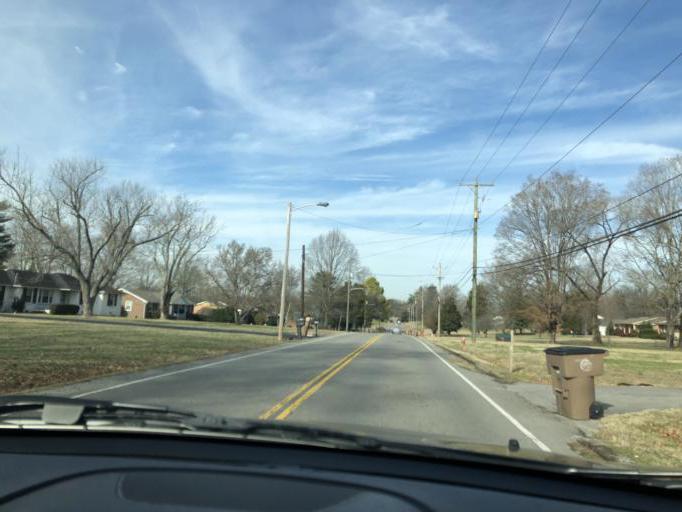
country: US
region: Tennessee
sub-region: Davidson County
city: Lakewood
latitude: 36.2041
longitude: -86.6786
